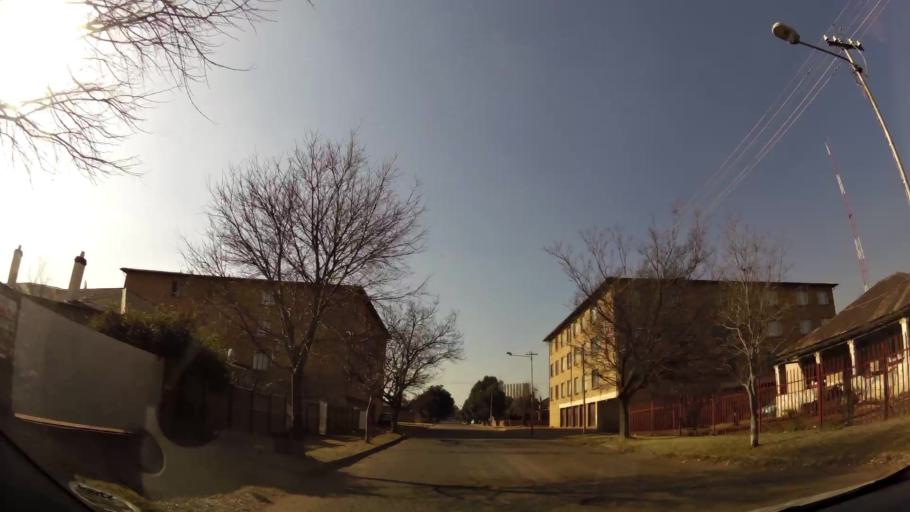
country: ZA
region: Gauteng
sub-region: West Rand District Municipality
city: Randfontein
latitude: -26.1723
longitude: 27.7076
